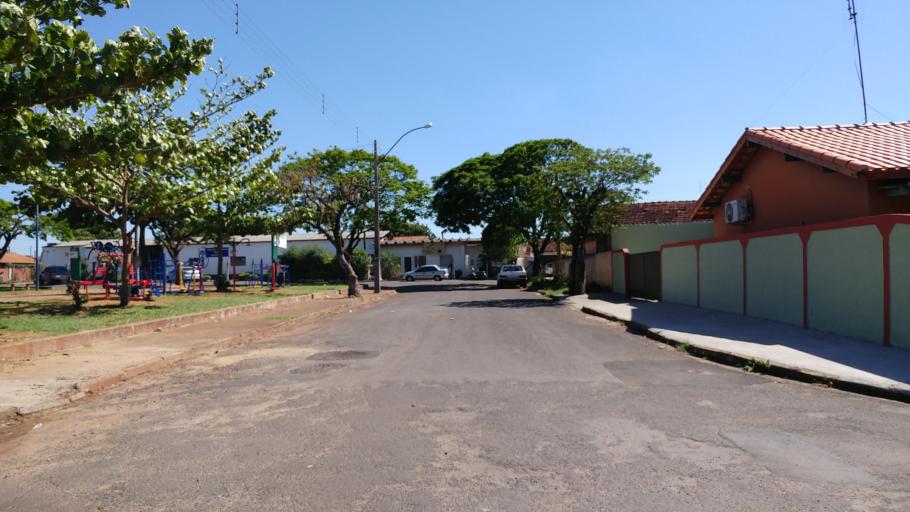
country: BR
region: Sao Paulo
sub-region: Paraguacu Paulista
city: Paraguacu Paulista
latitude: -22.4291
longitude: -50.5803
